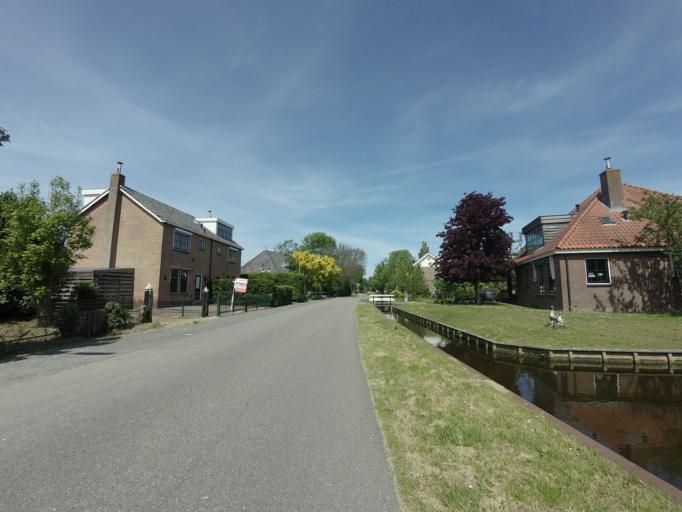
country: NL
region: North Holland
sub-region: Gemeente Velsen
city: Velsen-Zuid
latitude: 52.4497
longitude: 4.7235
